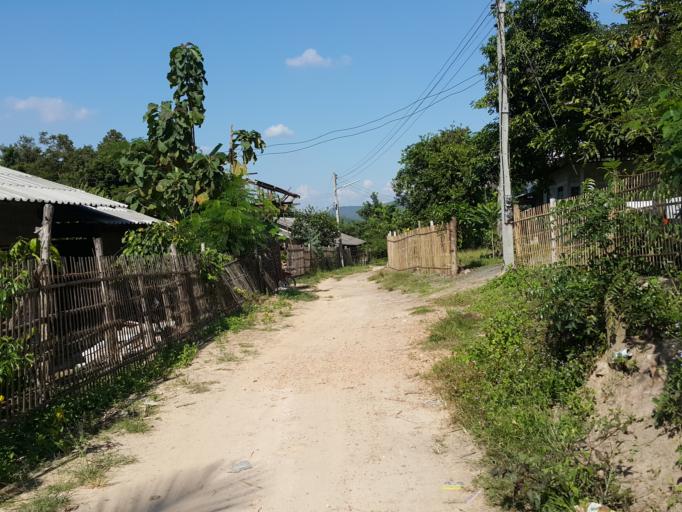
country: TH
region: Chiang Mai
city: San Kamphaeng
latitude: 18.7734
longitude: 99.1751
